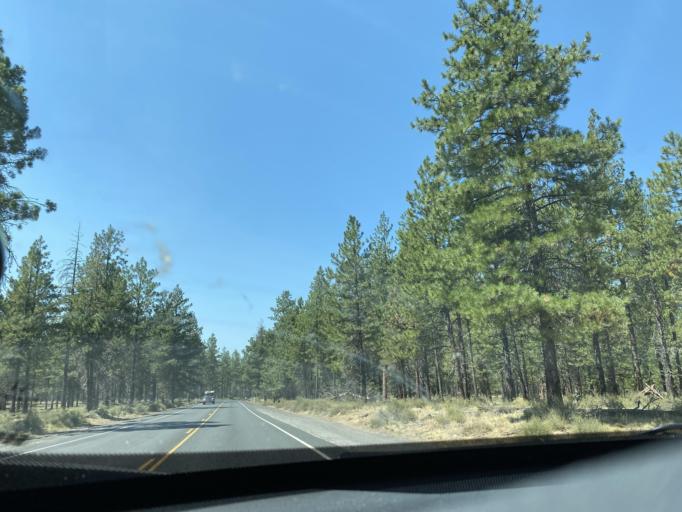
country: US
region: Oregon
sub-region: Deschutes County
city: Sunriver
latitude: 43.8896
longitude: -121.3932
